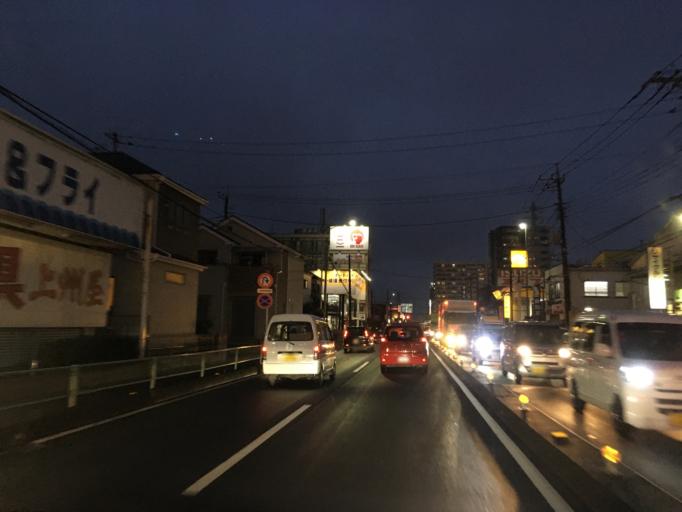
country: JP
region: Saitama
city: Shiki
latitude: 35.8002
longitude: 139.5605
